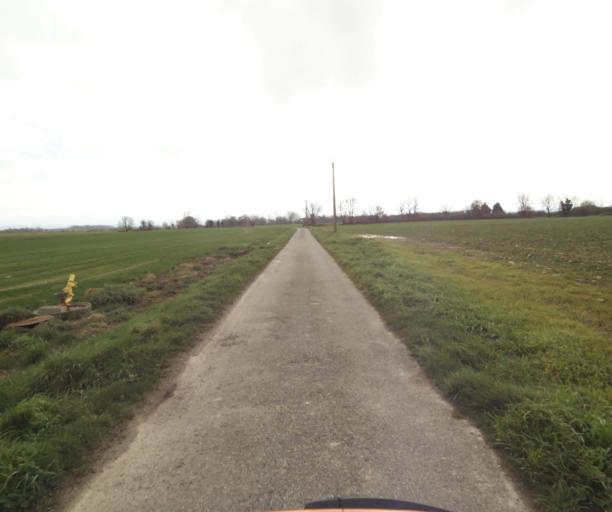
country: FR
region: Midi-Pyrenees
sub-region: Departement de l'Ariege
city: La Tour-du-Crieu
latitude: 43.1655
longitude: 1.6843
